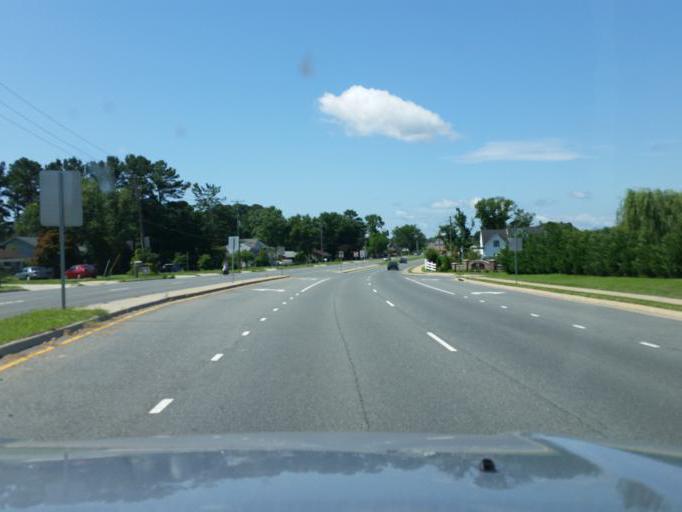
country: US
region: Virginia
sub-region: Stafford County
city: Falmouth
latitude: 38.3009
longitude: -77.5175
